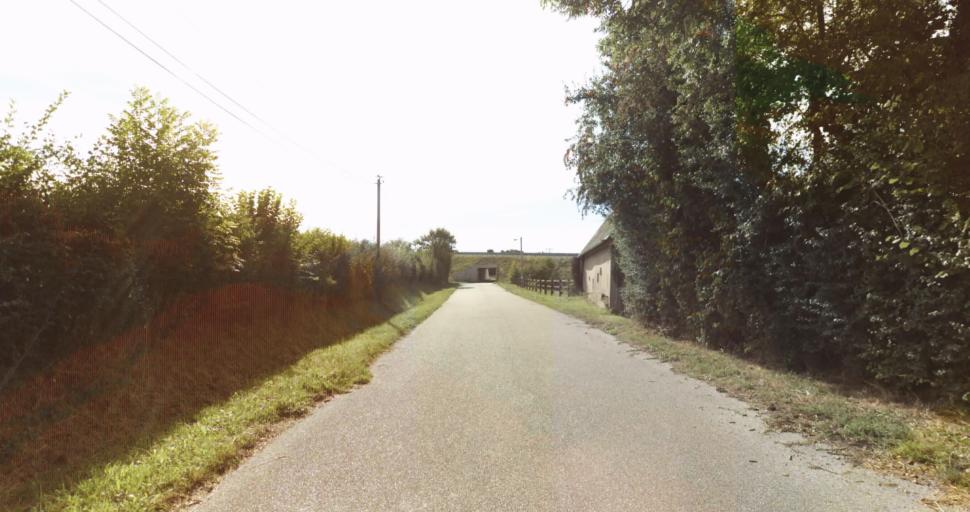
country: FR
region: Lower Normandy
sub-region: Departement de l'Orne
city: Sees
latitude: 48.7049
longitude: 0.2231
